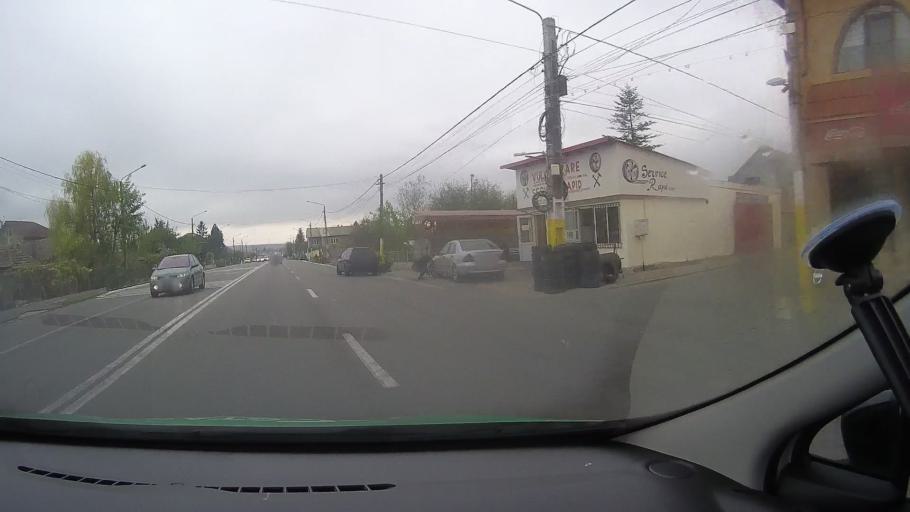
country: RO
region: Constanta
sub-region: Comuna Valu lui Traian
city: Valu lui Traian
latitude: 44.1678
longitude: 28.4515
